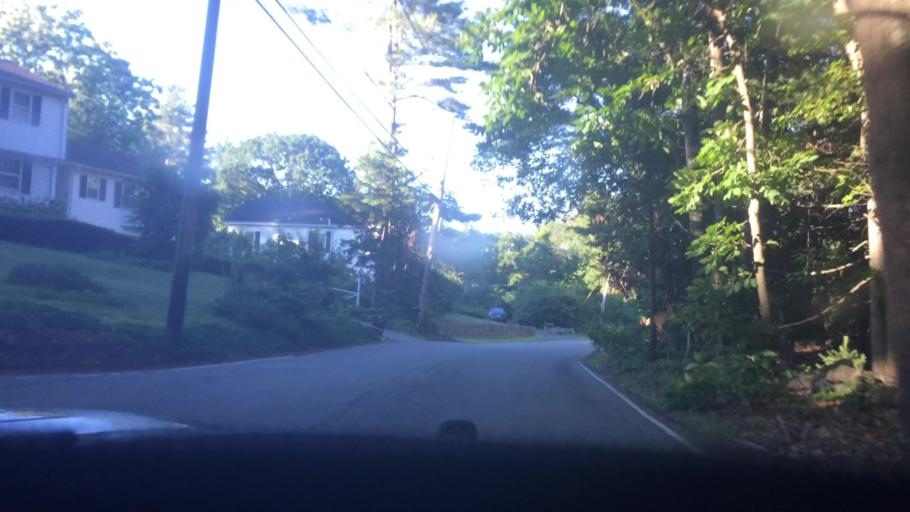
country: US
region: Massachusetts
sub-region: Essex County
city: Andover
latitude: 42.6397
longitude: -71.0877
